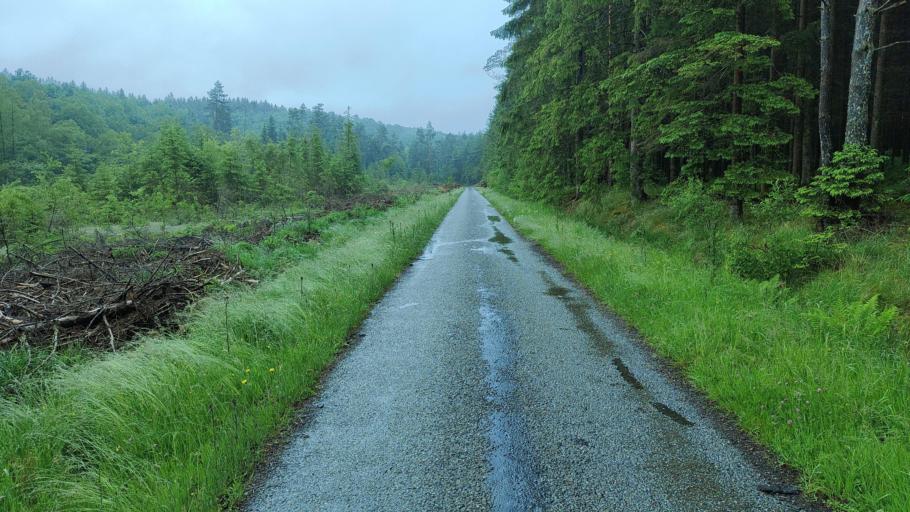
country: DE
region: North Rhine-Westphalia
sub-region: Regierungsbezirk Koln
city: Roetgen
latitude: 50.6401
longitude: 6.1617
